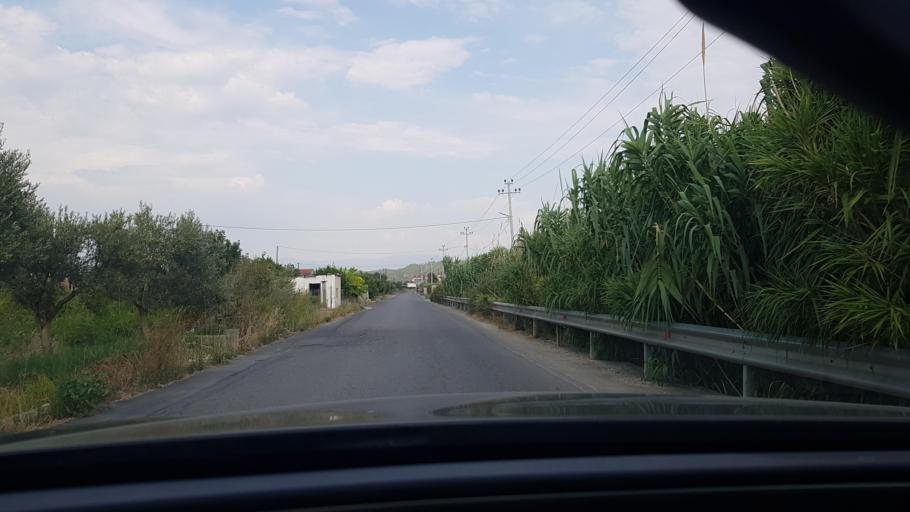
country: AL
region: Durres
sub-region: Rrethi i Durresit
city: Manze
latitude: 41.4729
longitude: 19.5440
